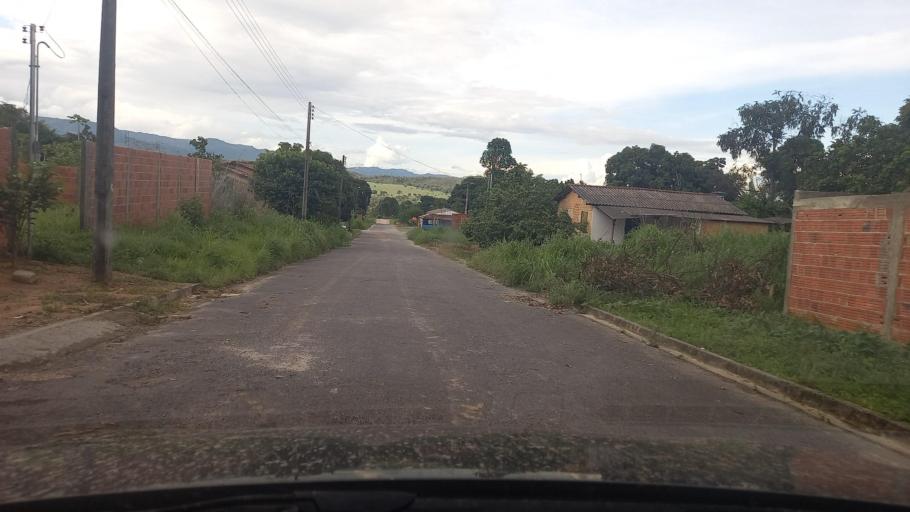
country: BR
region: Goias
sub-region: Cavalcante
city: Cavalcante
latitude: -13.7997
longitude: -47.4486
